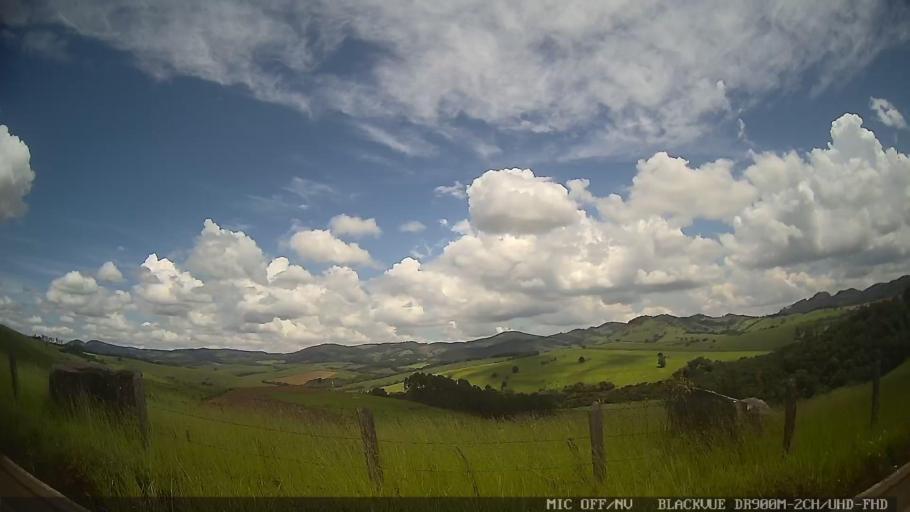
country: BR
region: Minas Gerais
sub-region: Extrema
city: Extrema
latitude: -22.7268
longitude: -46.4199
